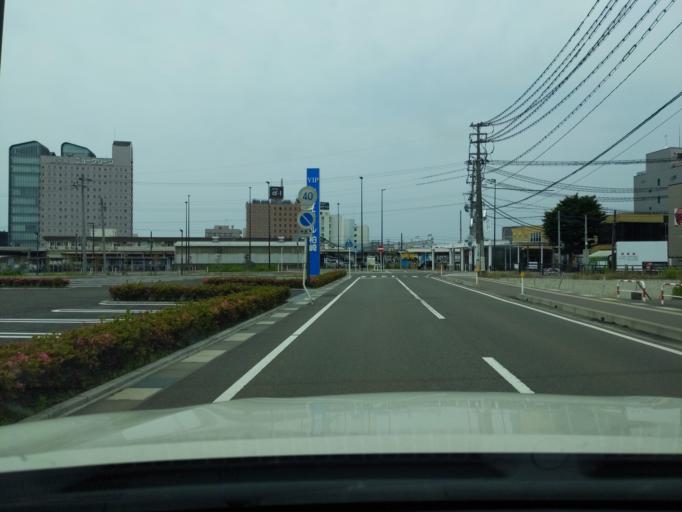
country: JP
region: Niigata
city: Kashiwazaki
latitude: 37.3619
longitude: 138.5563
